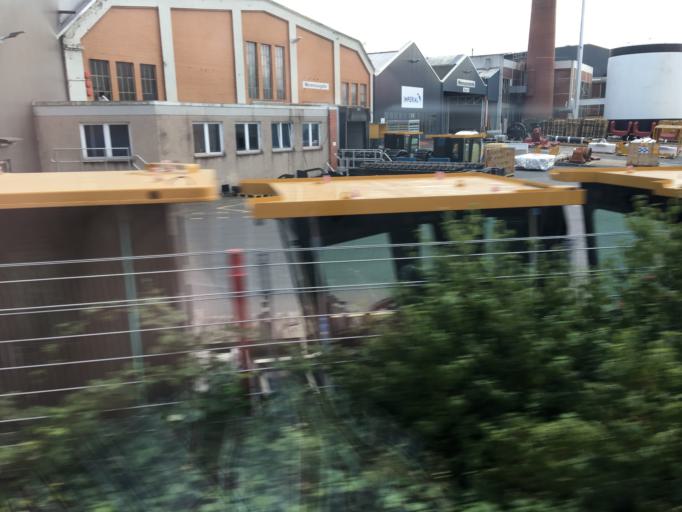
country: DE
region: North Rhine-Westphalia
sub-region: Regierungsbezirk Arnsberg
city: Dortmund
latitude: 51.5110
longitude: 7.4159
